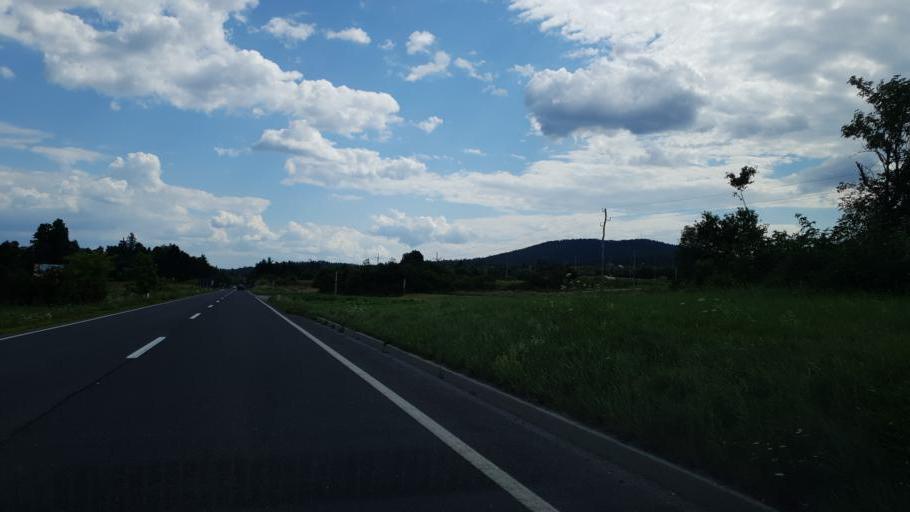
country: SI
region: Pivka
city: Pivka
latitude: 45.7130
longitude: 14.1906
